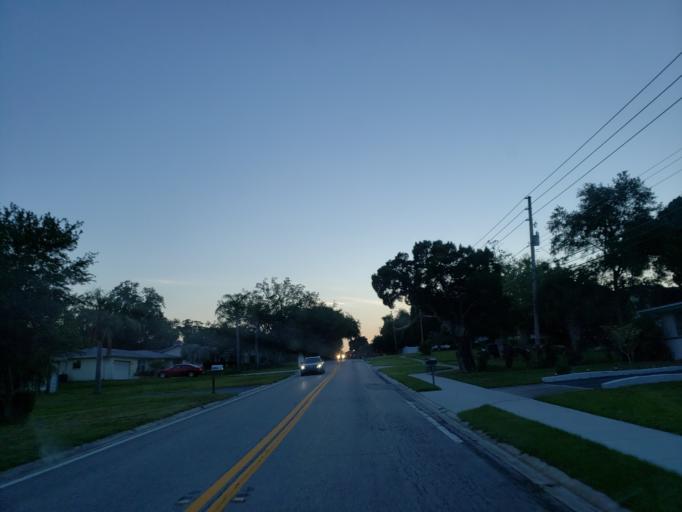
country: US
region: Florida
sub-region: Pinellas County
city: Harbor Bluffs
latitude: 27.9096
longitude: -82.8169
